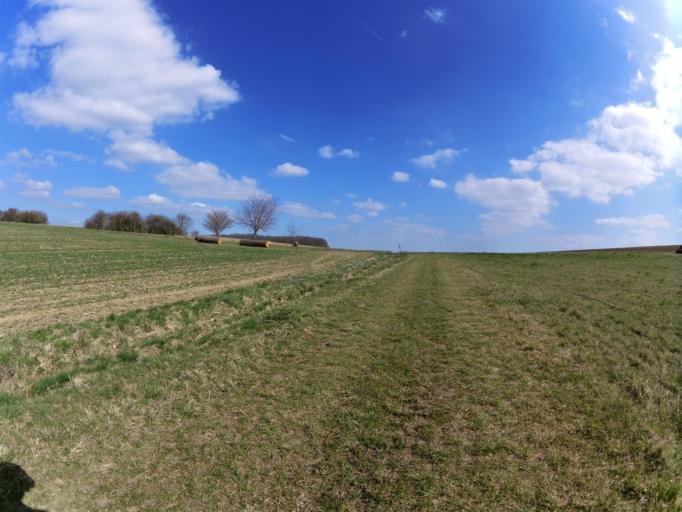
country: DE
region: Bavaria
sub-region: Regierungsbezirk Unterfranken
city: Nordheim
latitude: 49.8381
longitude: 10.1566
